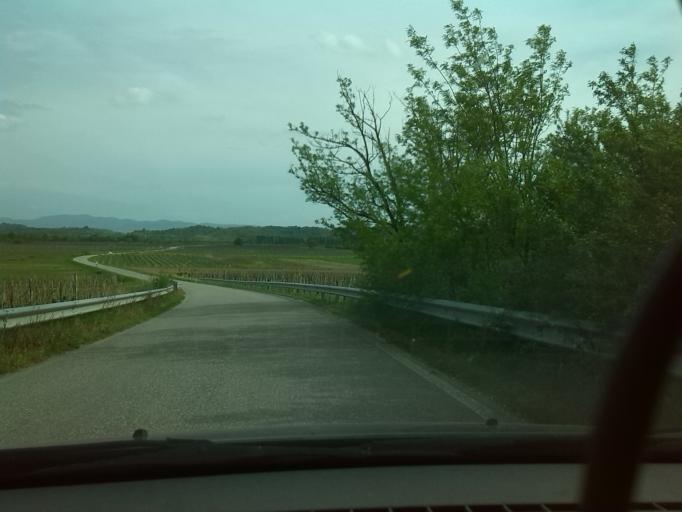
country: SI
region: Brda
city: Dobrovo
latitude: 45.9728
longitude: 13.5172
